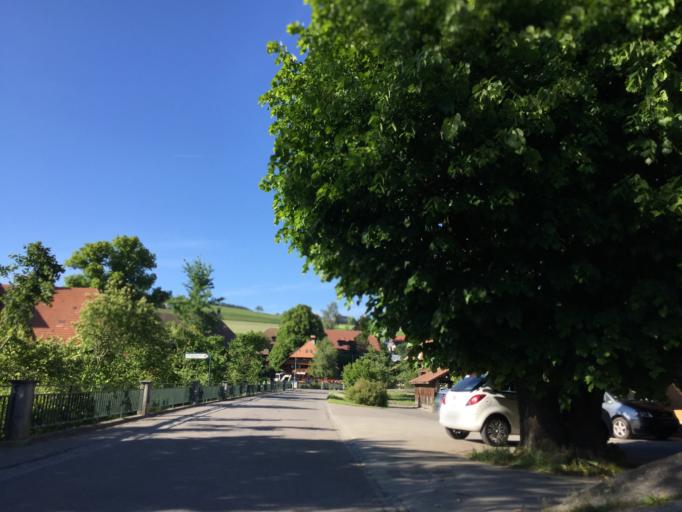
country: CH
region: Bern
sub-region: Bern-Mittelland District
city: Zaziwil
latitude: 46.8948
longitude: 7.6469
